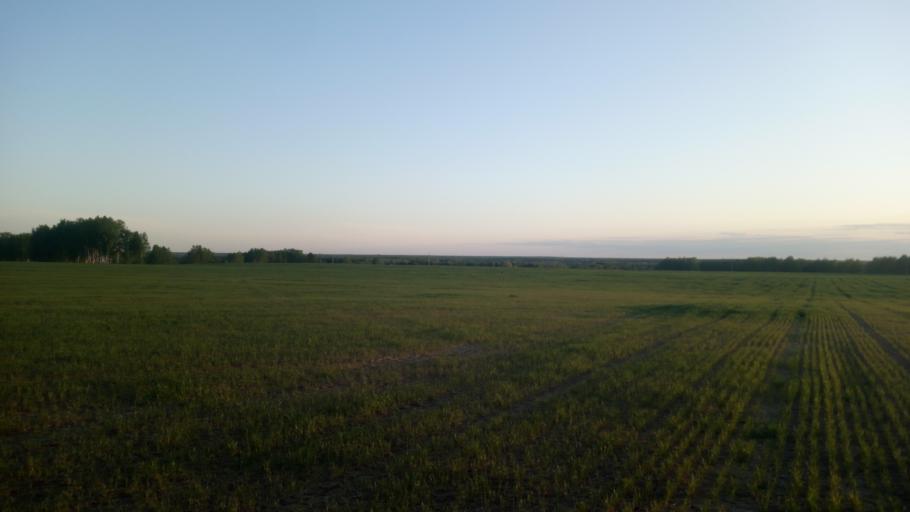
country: RU
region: Mariy-El
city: Orshanka
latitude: 56.8332
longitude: 48.0007
